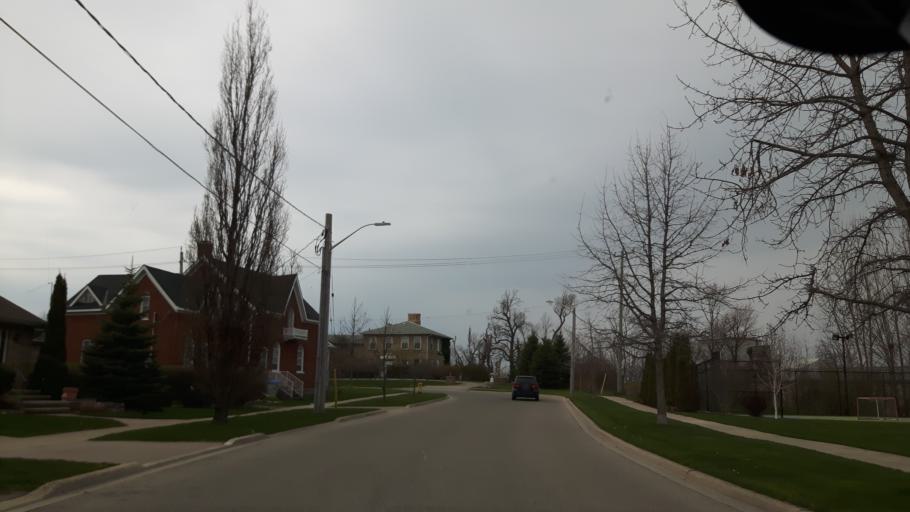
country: CA
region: Ontario
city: Goderich
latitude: 43.7448
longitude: -81.7169
